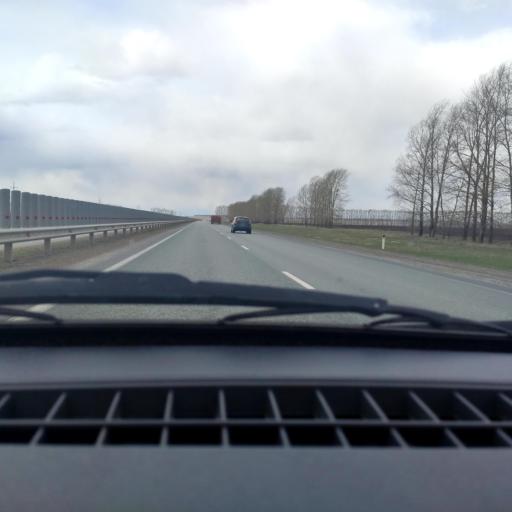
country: RU
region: Bashkortostan
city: Asanovo
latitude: 54.9899
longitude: 55.5145
